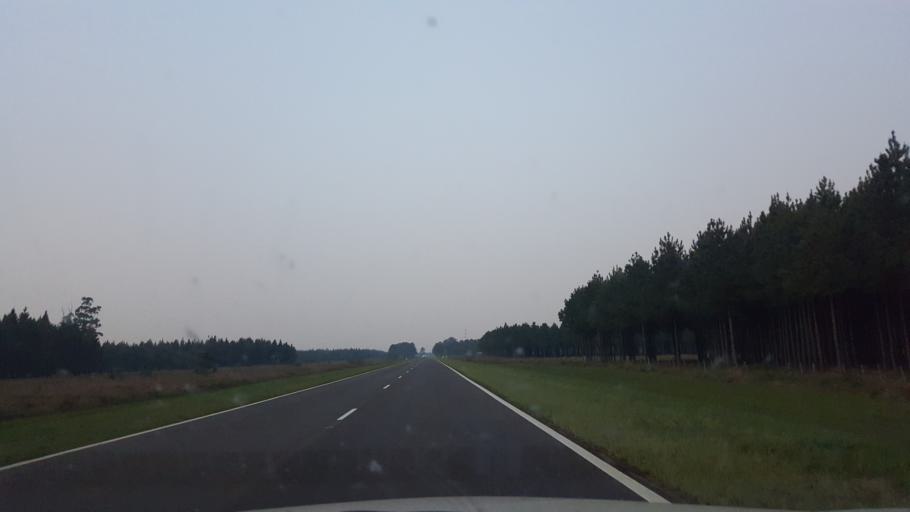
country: PY
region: Misiones
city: Ayolas
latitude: -27.6236
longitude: -56.9376
